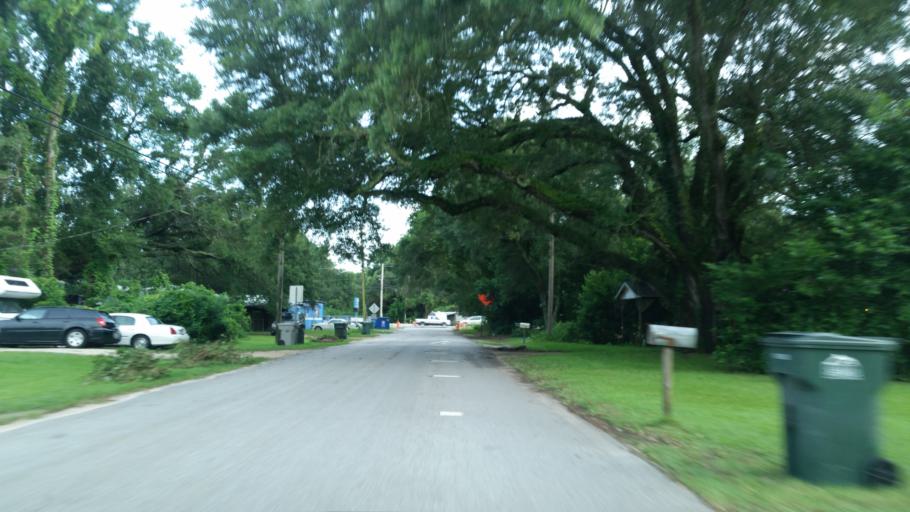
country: US
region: Florida
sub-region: Escambia County
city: Ferry Pass
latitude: 30.5113
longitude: -87.2129
